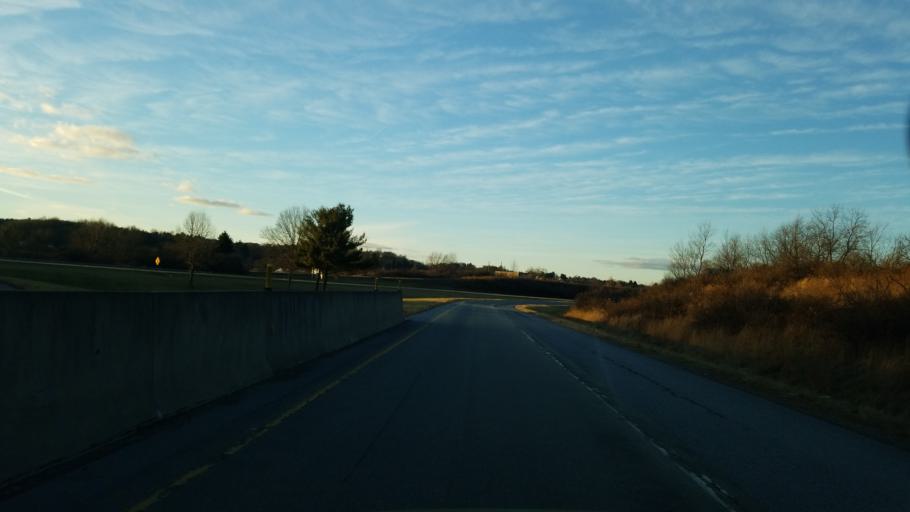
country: US
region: Pennsylvania
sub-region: Indiana County
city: Chevy Chase Heights
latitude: 40.6292
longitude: -79.1153
